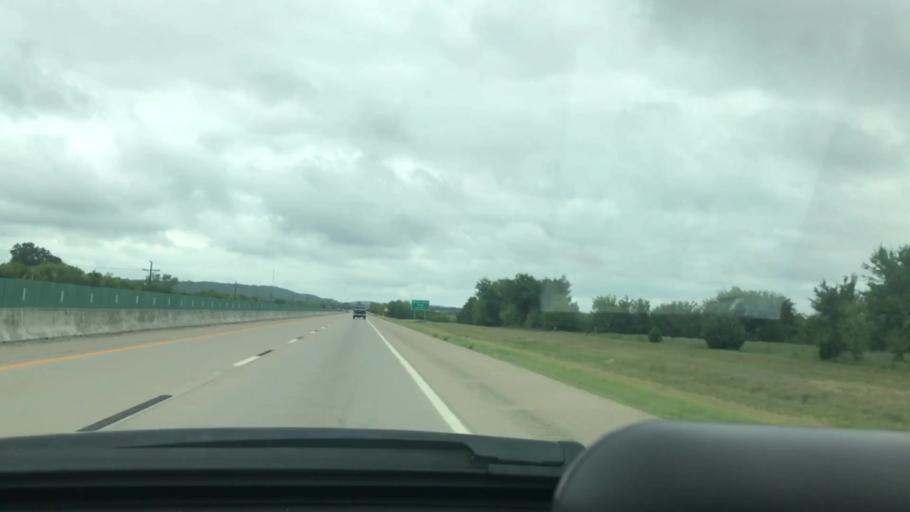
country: US
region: Oklahoma
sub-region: Pittsburg County
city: Krebs
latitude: 35.0385
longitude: -95.7119
